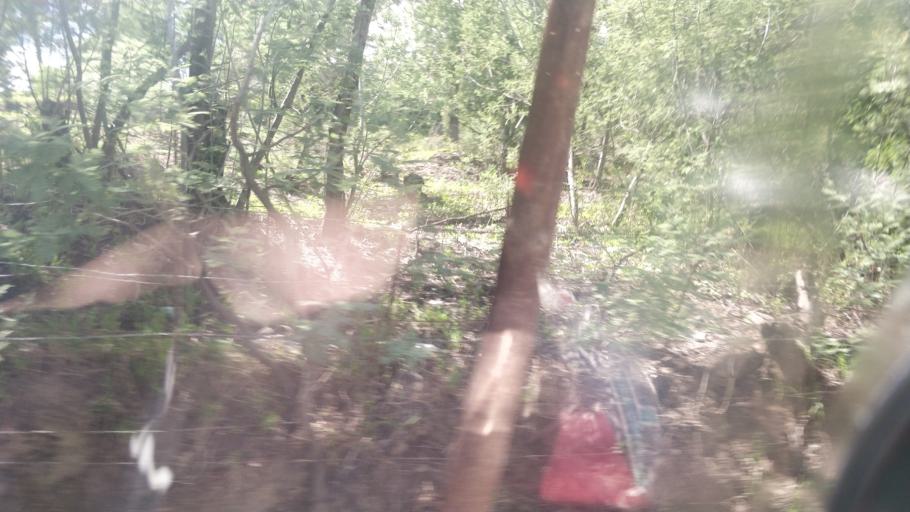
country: LS
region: Maseru
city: Nako
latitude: -29.6269
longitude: 27.5089
